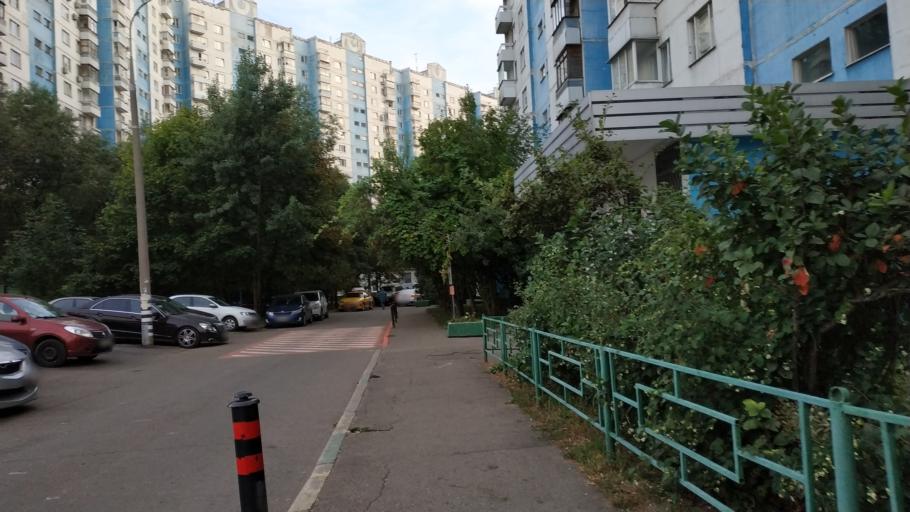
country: RU
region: Moscow
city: Solntsevo
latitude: 55.6434
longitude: 37.3687
